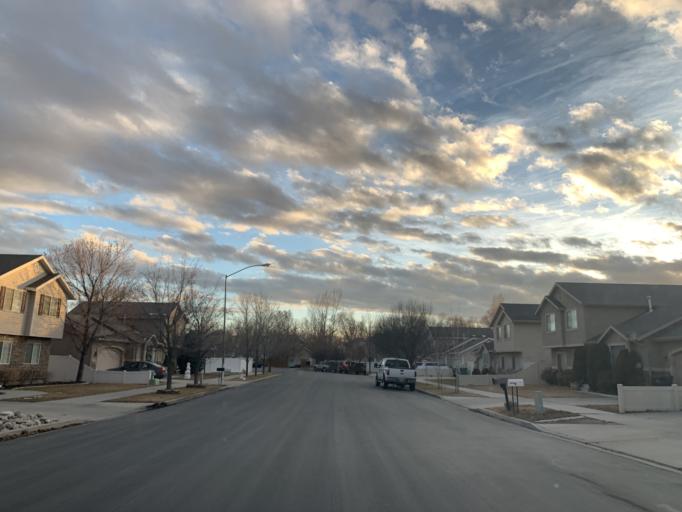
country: US
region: Utah
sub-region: Utah County
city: Provo
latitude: 40.2407
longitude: -111.7094
